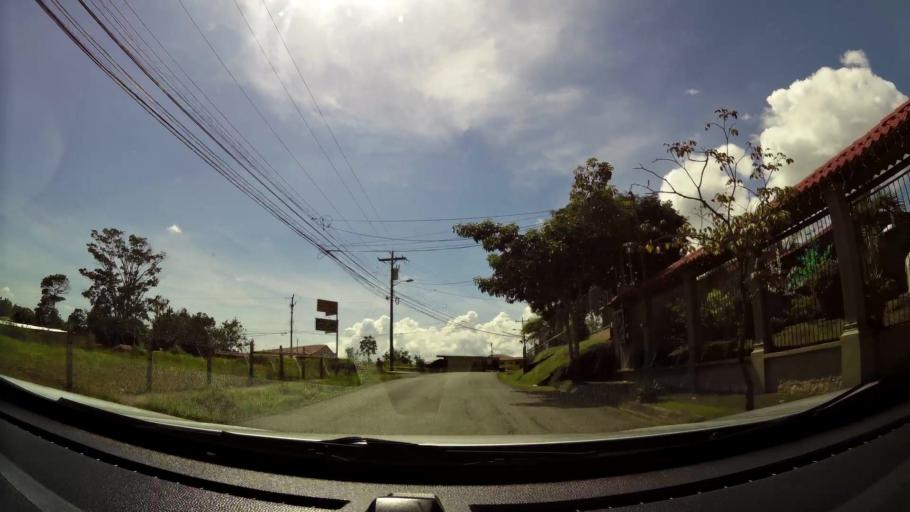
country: CR
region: San Jose
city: San Isidro
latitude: 9.3809
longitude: -83.6973
